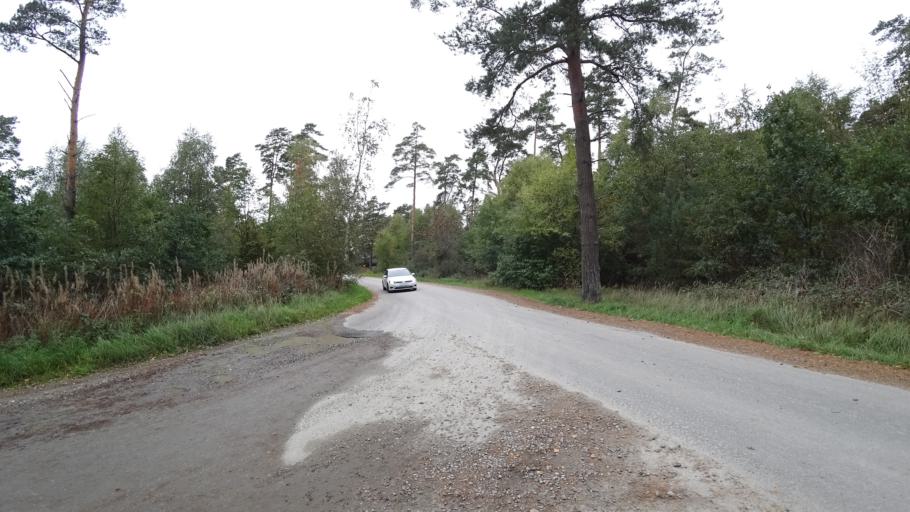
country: SE
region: Skane
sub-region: Kavlinge Kommun
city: Hofterup
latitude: 55.8245
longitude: 12.9492
